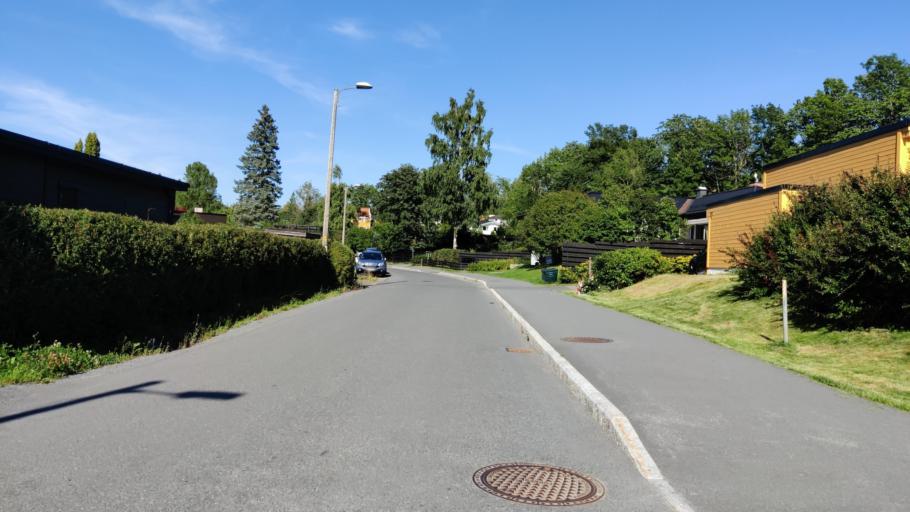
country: NO
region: Akershus
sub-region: Baerum
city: Lysaker
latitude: 59.9290
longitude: 10.6021
